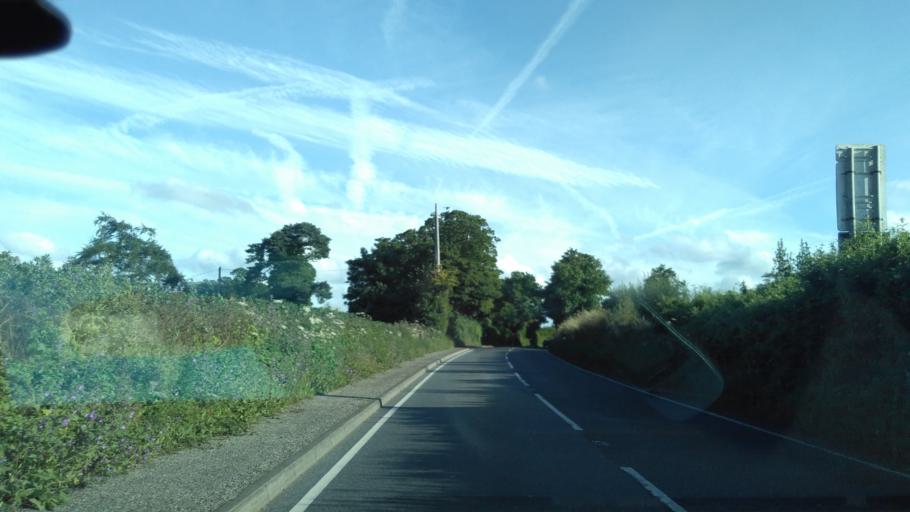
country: GB
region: England
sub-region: Kent
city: Faversham
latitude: 51.2963
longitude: 0.8895
